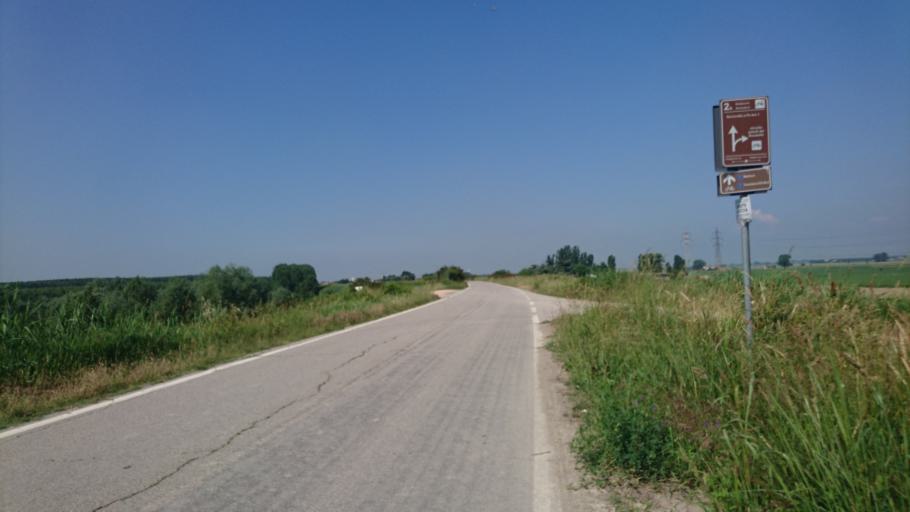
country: IT
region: Lombardy
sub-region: Provincia di Mantova
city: Ostiglia
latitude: 45.0757
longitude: 11.1124
